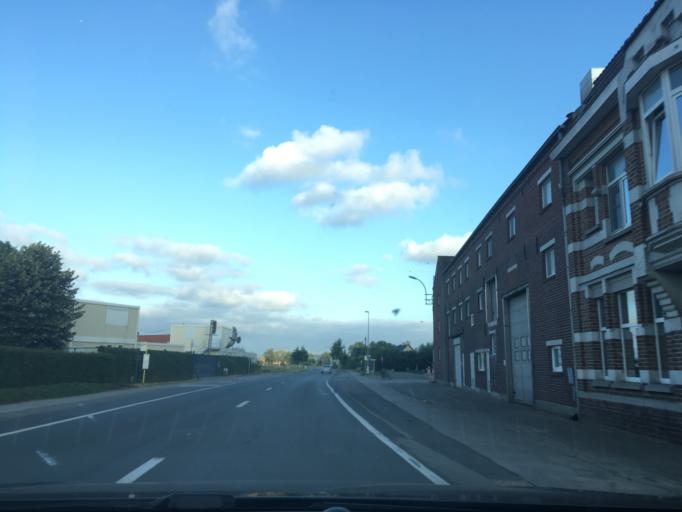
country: BE
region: Flanders
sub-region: Provincie West-Vlaanderen
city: Wingene
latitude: 51.0471
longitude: 3.2965
